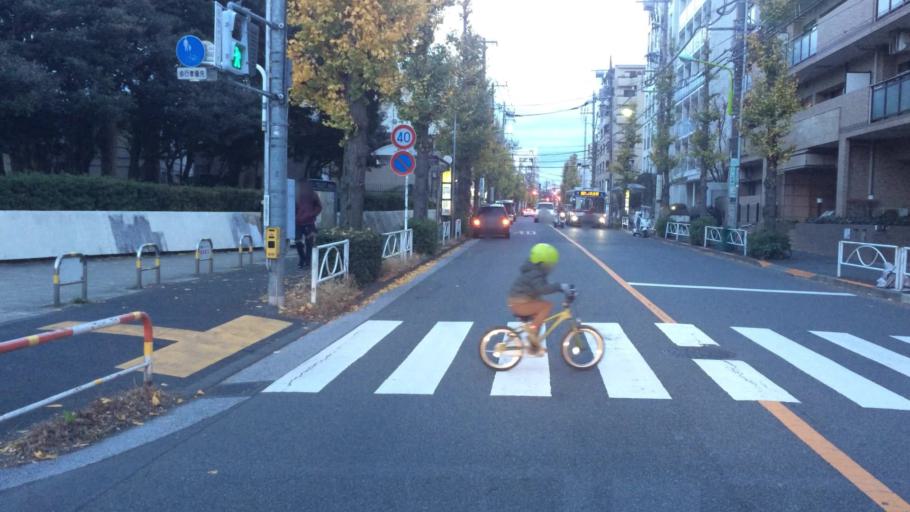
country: JP
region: Tokyo
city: Tokyo
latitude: 35.6280
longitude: 139.6562
